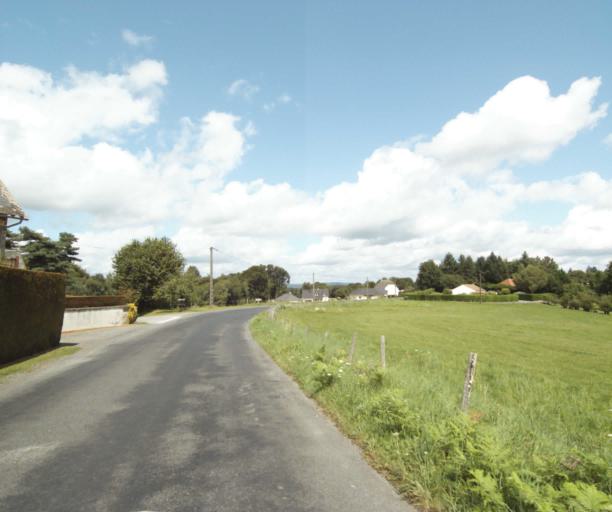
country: FR
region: Limousin
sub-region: Departement de la Correze
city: Sainte-Fortunade
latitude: 45.1993
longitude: 1.8247
